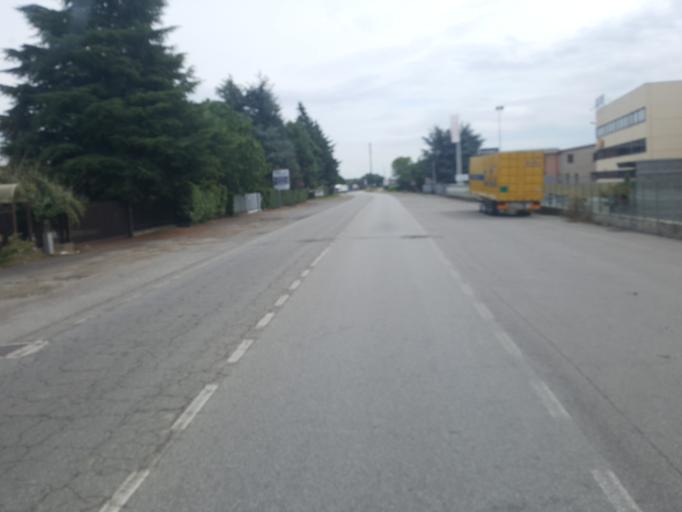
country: IT
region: Lombardy
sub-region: Citta metropolitana di Milano
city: Cambiago
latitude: 45.5801
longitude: 9.4341
